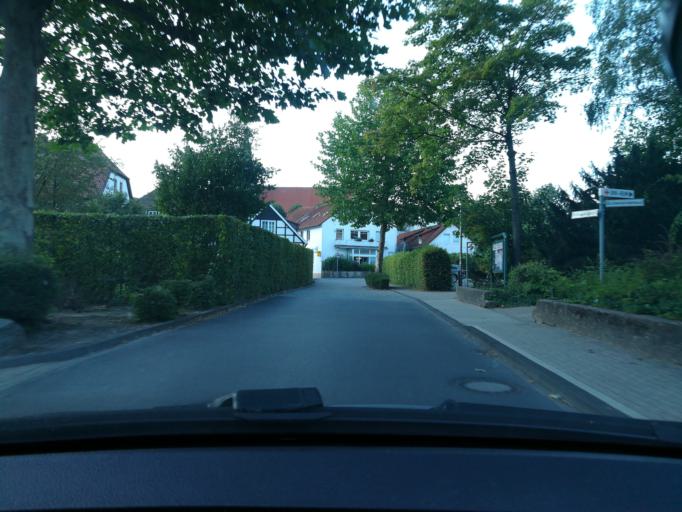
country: DE
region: North Rhine-Westphalia
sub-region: Regierungsbezirk Munster
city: Lienen
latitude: 52.1455
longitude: 7.9749
